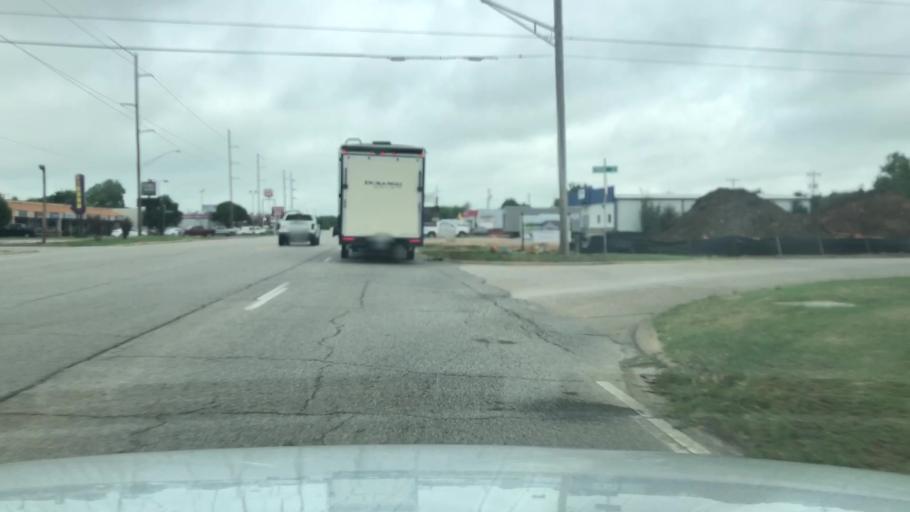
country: US
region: Oklahoma
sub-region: Washington County
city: Bartlesville
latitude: 36.7281
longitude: -95.9306
